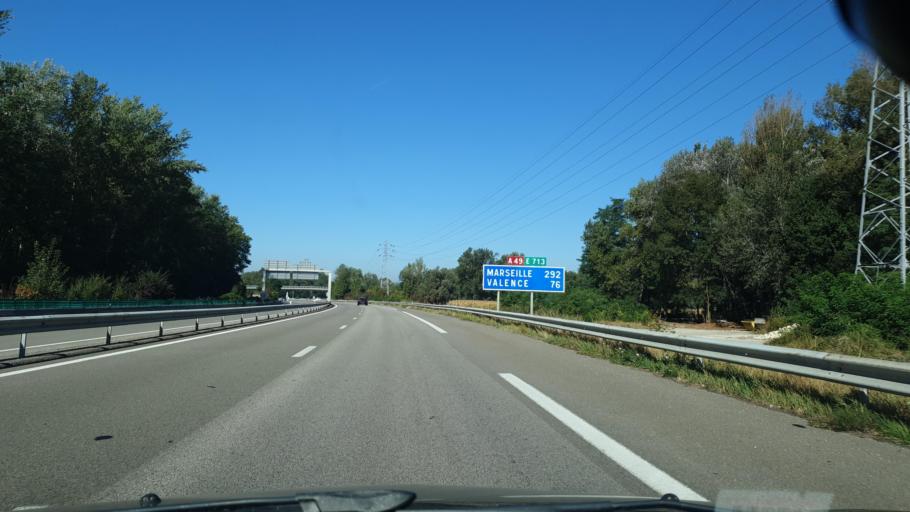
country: FR
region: Rhone-Alpes
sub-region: Departement de l'Isere
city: Voreppe
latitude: 45.3033
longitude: 5.6108
